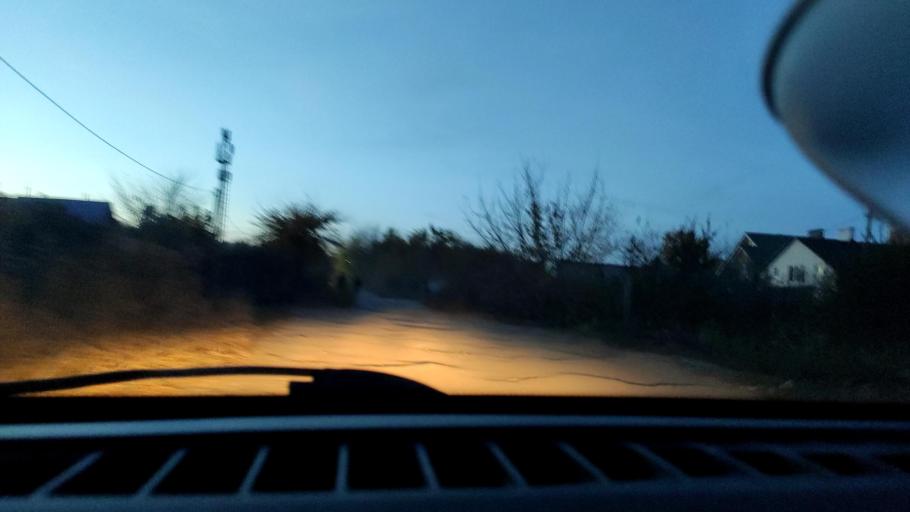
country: RU
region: Samara
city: Samara
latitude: 53.2234
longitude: 50.2136
